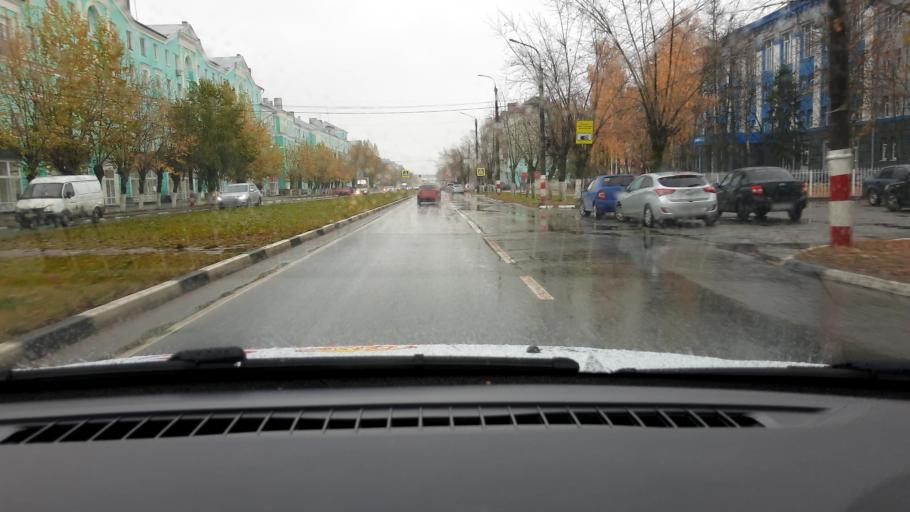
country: RU
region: Nizjnij Novgorod
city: Dzerzhinsk
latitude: 56.2412
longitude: 43.4471
